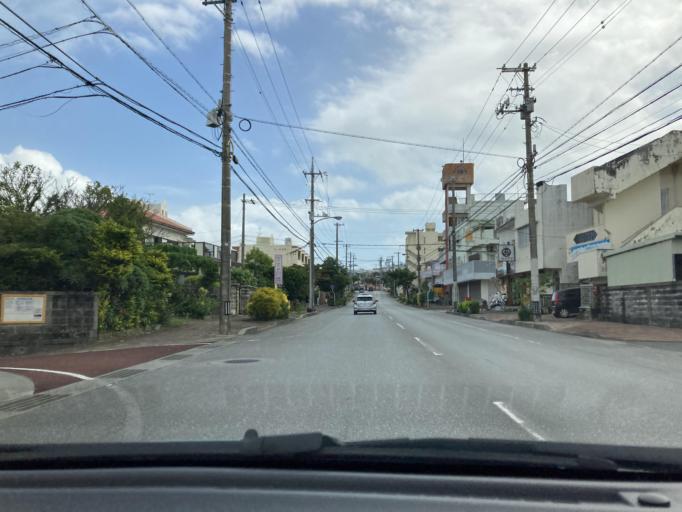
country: JP
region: Okinawa
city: Ginowan
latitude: 26.2625
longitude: 127.7466
